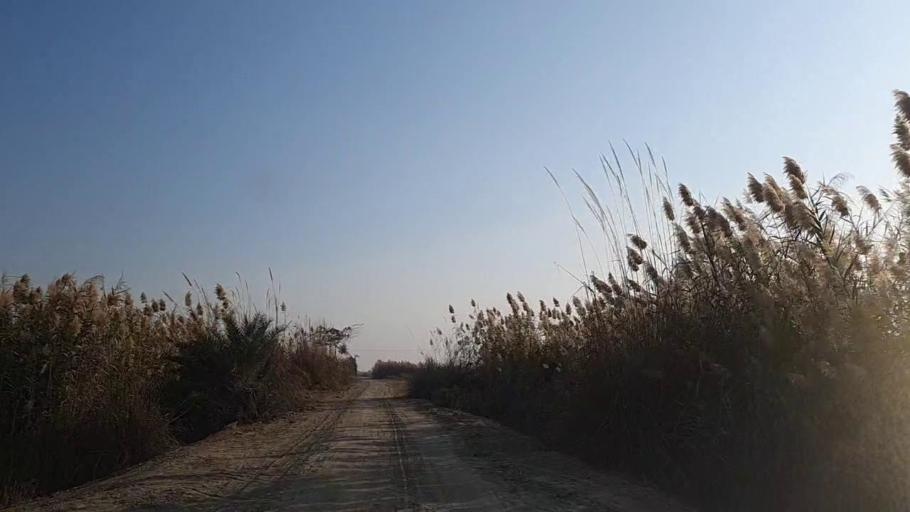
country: PK
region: Sindh
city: Daur
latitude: 26.4326
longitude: 68.3527
